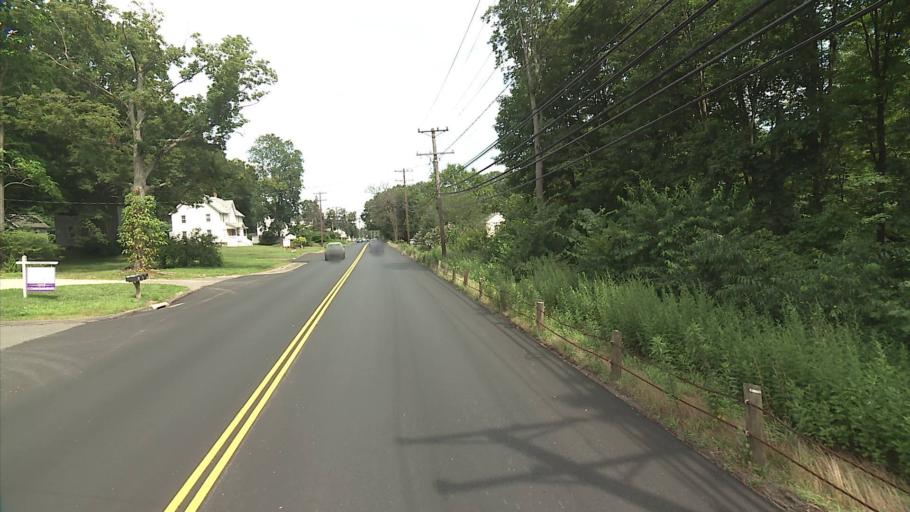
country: US
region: Connecticut
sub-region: New Haven County
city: Seymour
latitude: 41.4015
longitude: -73.0901
